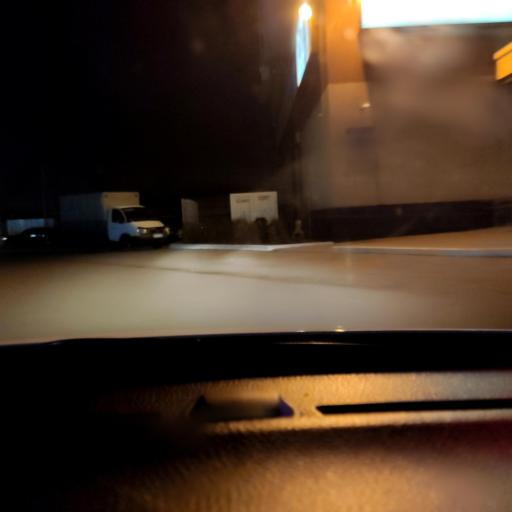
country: RU
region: Voronezj
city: Novaya Usman'
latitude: 51.6434
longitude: 39.4094
